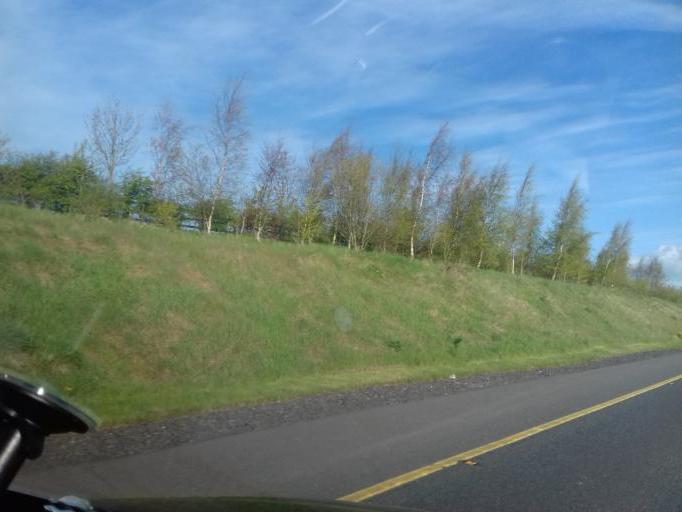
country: IE
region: Leinster
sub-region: An Mhi
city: Navan
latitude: 53.6599
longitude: -6.7574
